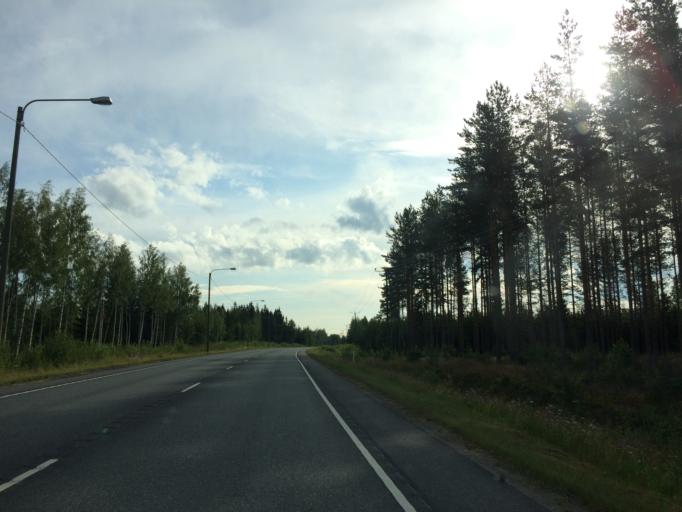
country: FI
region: Haeme
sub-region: Haemeenlinna
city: Janakkala
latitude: 60.9199
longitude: 24.5773
